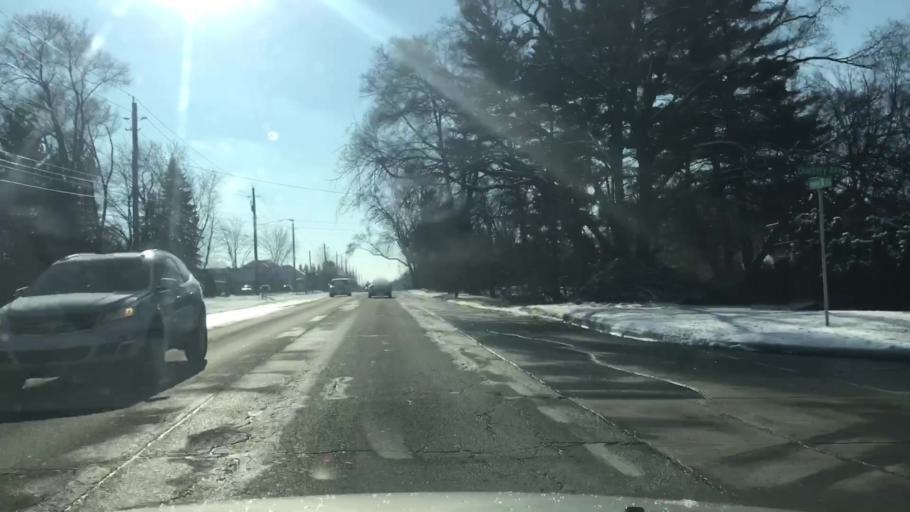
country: US
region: Michigan
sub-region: Oakland County
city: Troy
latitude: 42.6198
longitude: -83.1107
